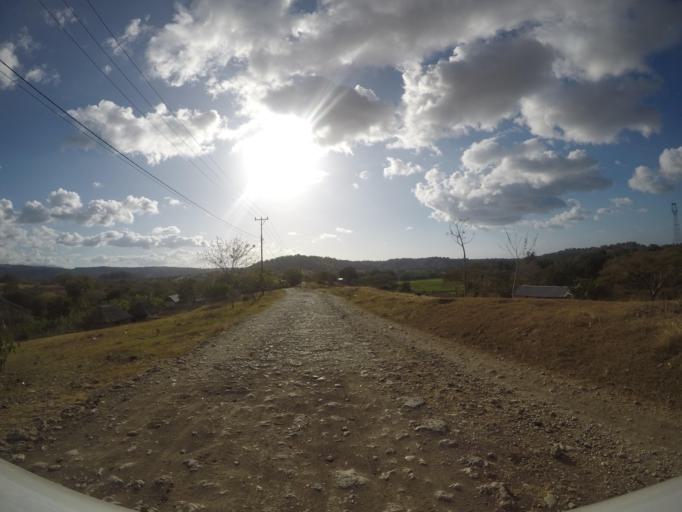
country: TL
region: Lautem
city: Lospalos
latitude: -8.4280
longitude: 126.8385
